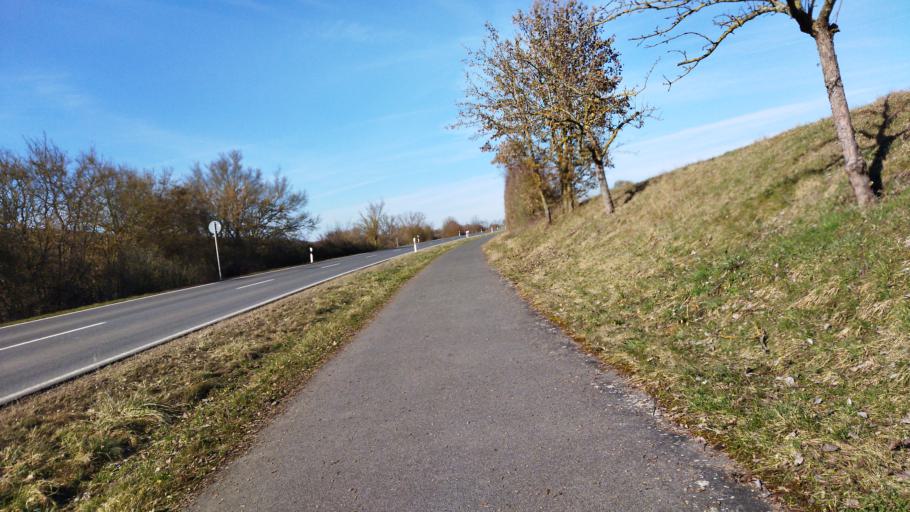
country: DE
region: Bavaria
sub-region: Regierungsbezirk Unterfranken
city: Wipfeld
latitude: 49.9283
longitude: 10.1840
